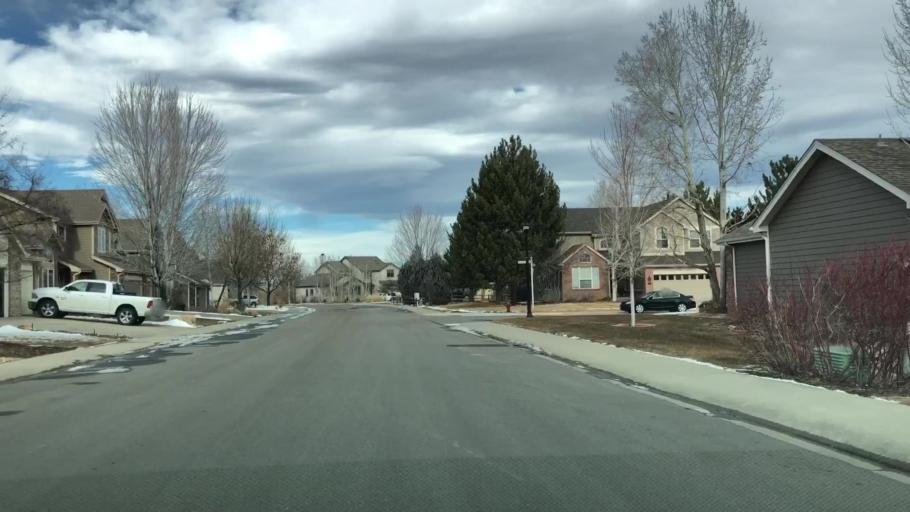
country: US
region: Colorado
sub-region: Weld County
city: Windsor
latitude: 40.4723
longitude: -104.9464
